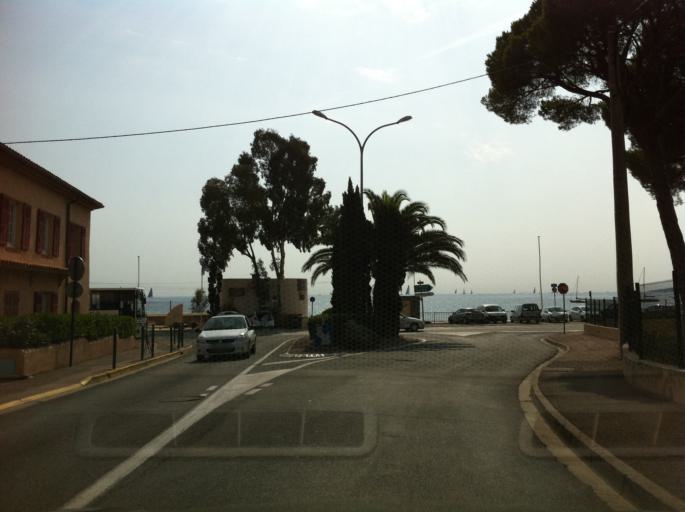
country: FR
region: Provence-Alpes-Cote d'Azur
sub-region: Departement du Var
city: Sainte-Maxime
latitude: 43.3413
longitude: 6.6801
